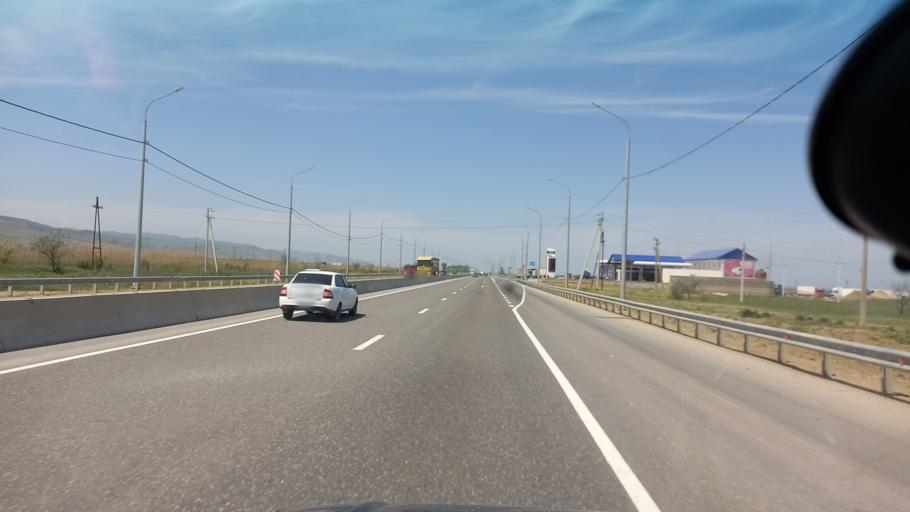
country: RU
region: Dagestan
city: Manas
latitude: 42.7405
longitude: 47.6598
